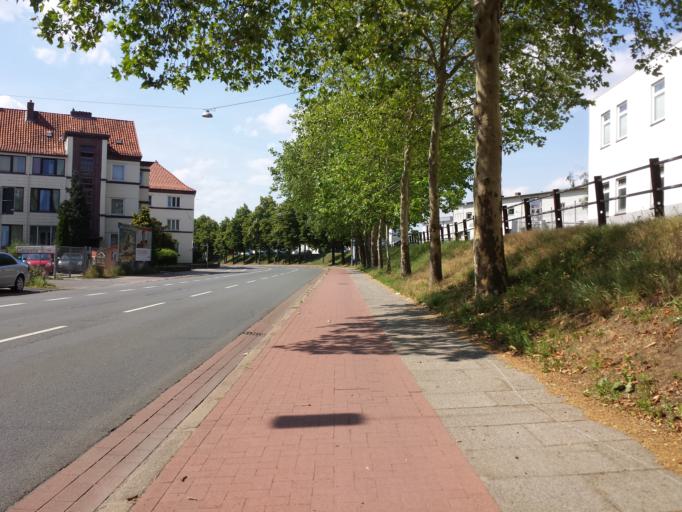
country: DE
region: Bremen
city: Bremen
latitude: 53.0772
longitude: 8.7824
